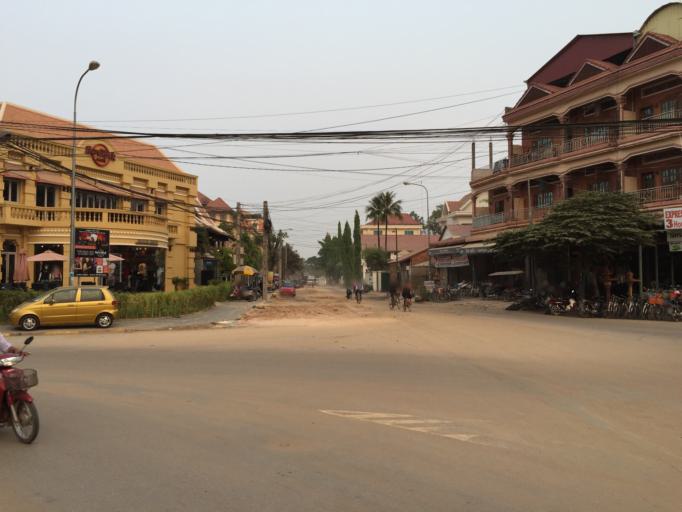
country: KH
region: Siem Reap
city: Siem Reap
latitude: 13.3530
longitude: 103.8564
